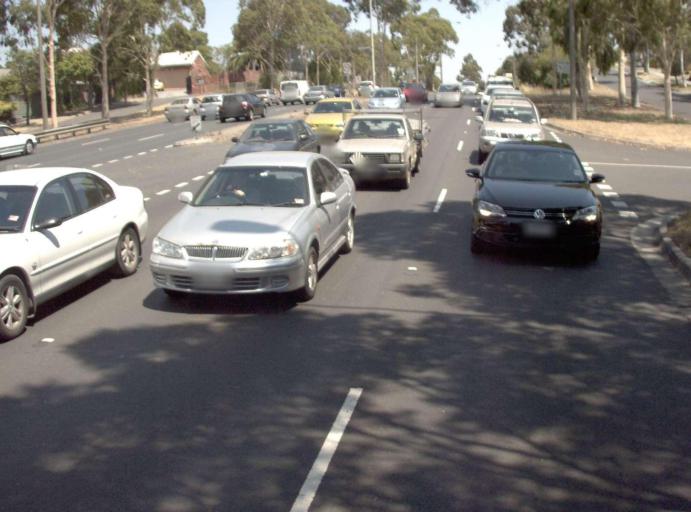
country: AU
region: Victoria
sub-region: Whitehorse
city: Vermont South
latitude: -37.8662
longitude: 145.1683
